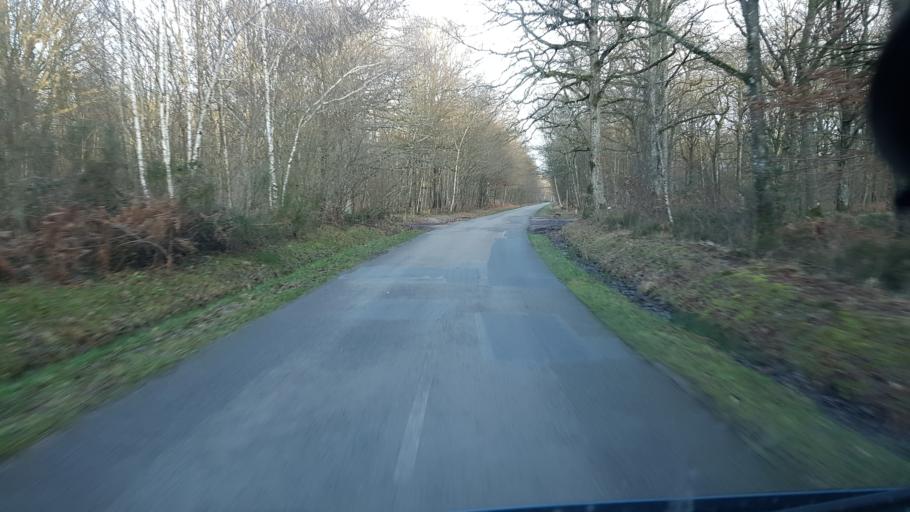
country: FR
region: Ile-de-France
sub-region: Departement des Yvelines
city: Saint-Leger-en-Yvelines
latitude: 48.6955
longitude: 1.7973
